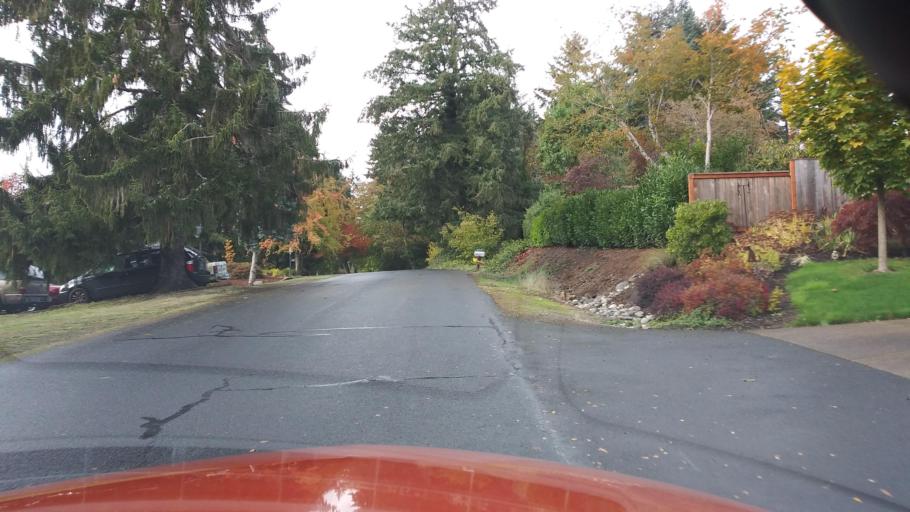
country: US
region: Oregon
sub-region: Washington County
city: Forest Grove
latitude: 45.5328
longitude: -123.1360
